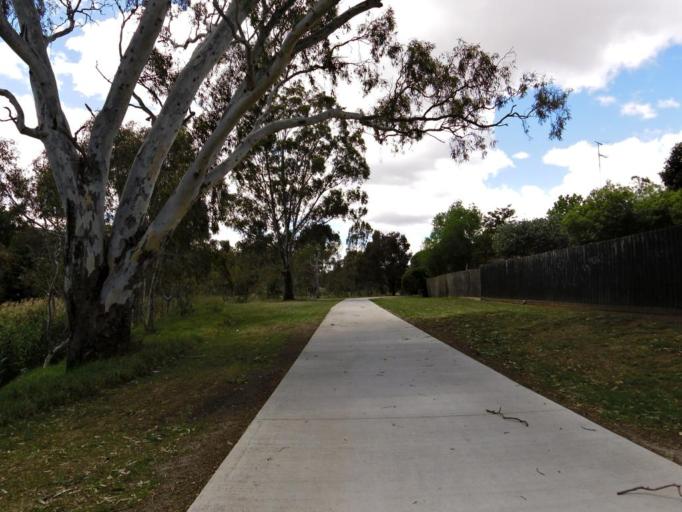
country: AU
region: Victoria
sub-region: Hume
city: Westmeadows
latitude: -37.6818
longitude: 144.8986
